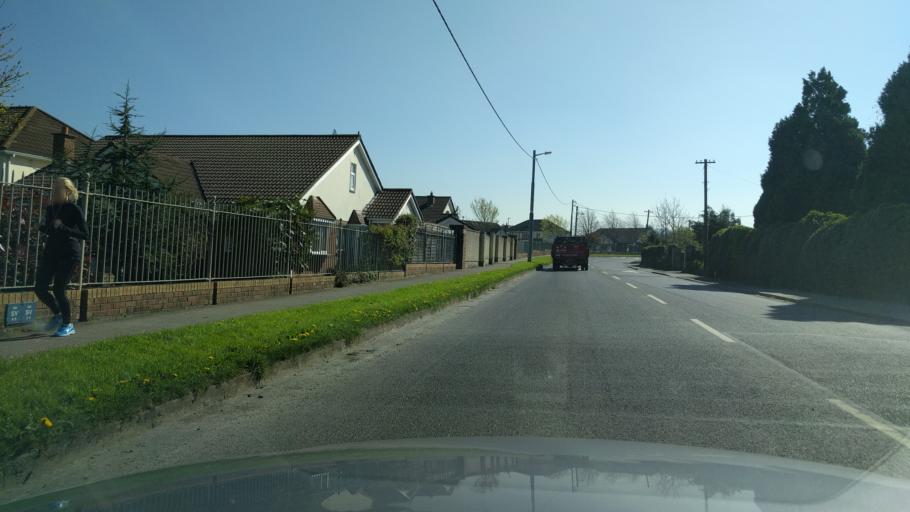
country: IE
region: Leinster
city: Firhouse
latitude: 53.2714
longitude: -6.3466
